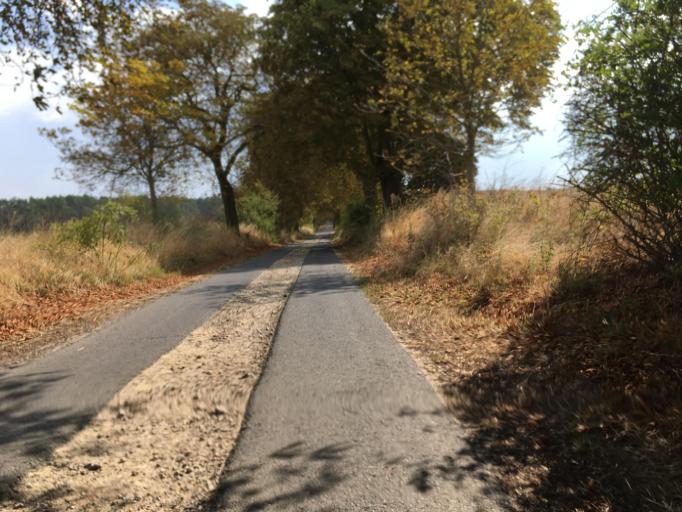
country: DE
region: Brandenburg
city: Zehdenick
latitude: 53.0793
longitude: 13.2858
